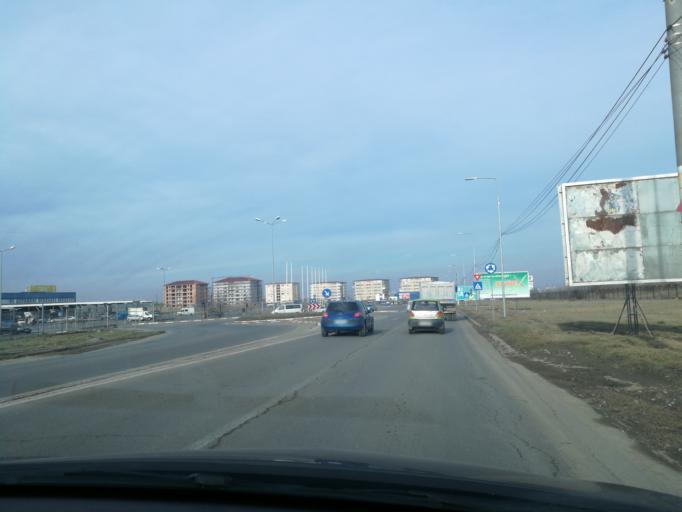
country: RO
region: Constanta
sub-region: Municipiul Constanta
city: Palazu Mare
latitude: 44.1959
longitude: 28.6043
